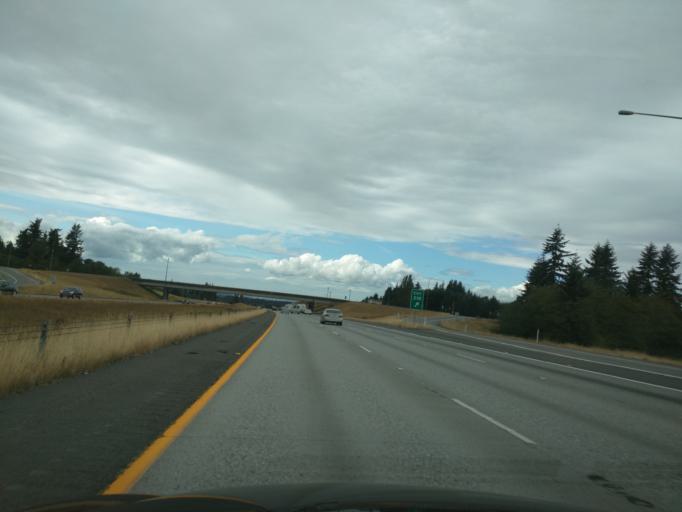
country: US
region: Washington
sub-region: Snohomish County
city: Stanwood
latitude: 48.3059
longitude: -122.3133
